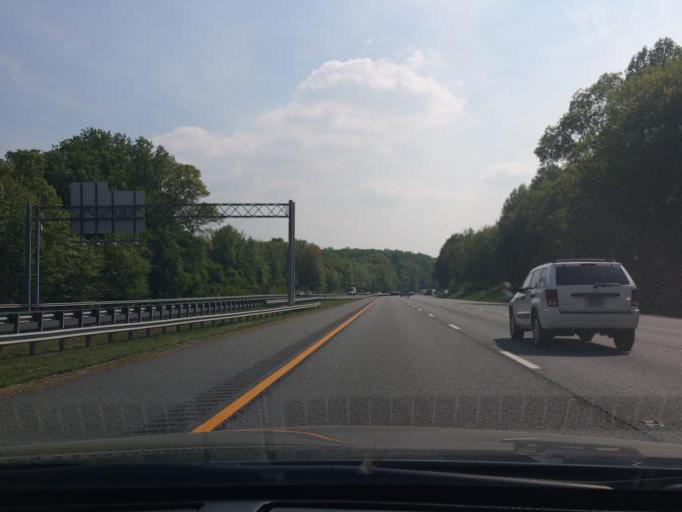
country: US
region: Maryland
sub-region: Harford County
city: Havre de Grace
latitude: 39.5667
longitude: -76.1421
